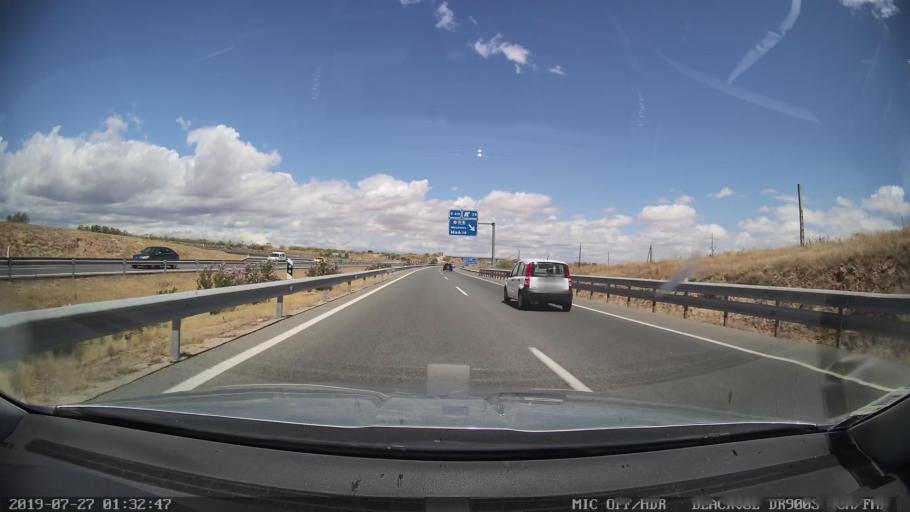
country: ES
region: Castille-La Mancha
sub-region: Province of Toledo
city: Valmojado
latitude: 40.2246
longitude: -4.0734
